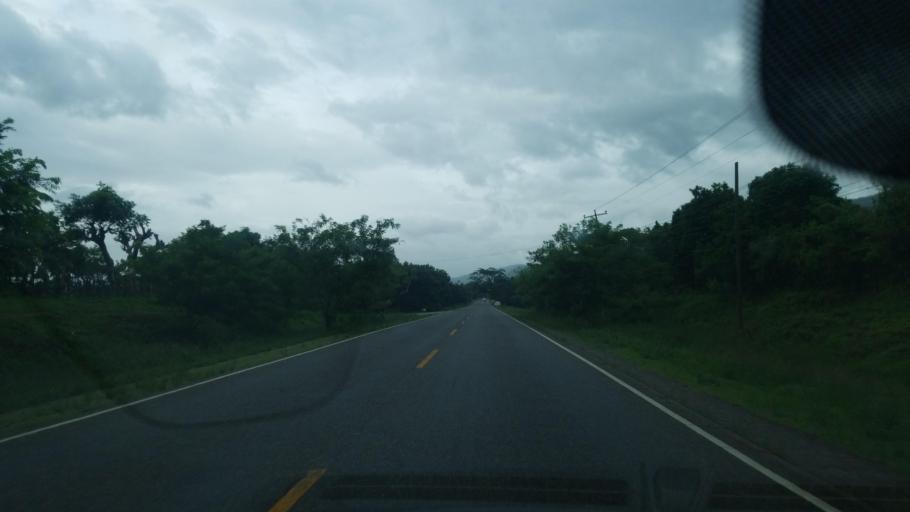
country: HN
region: Ocotepeque
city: Antigua Ocotepeque
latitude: 14.3904
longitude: -89.2042
